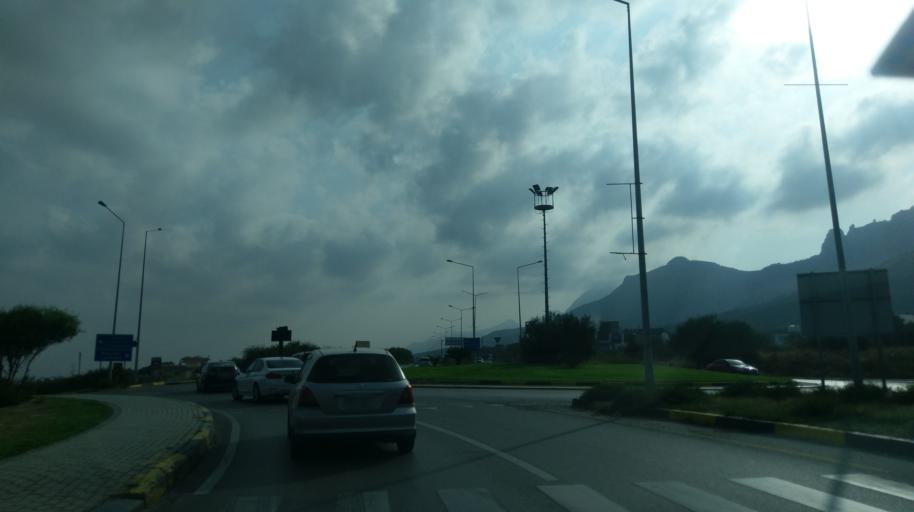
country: CY
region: Keryneia
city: Kyrenia
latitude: 35.3314
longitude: 33.2744
